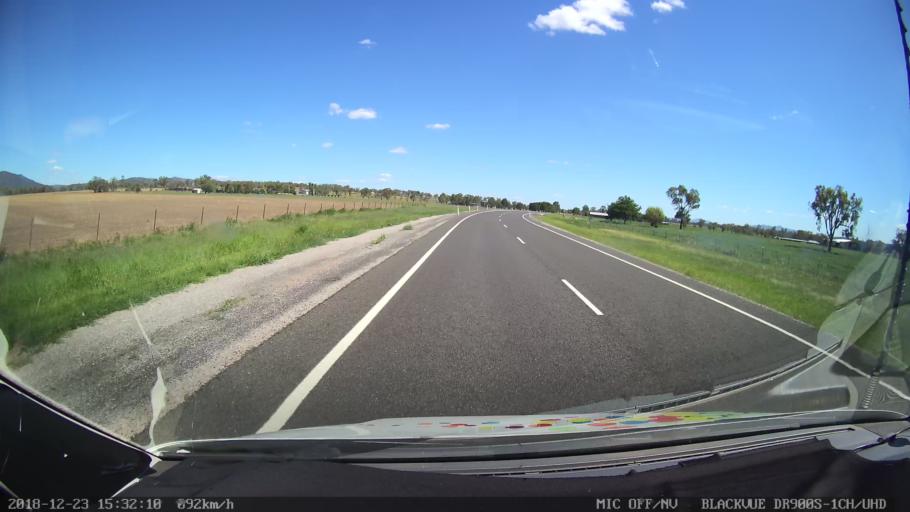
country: AU
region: New South Wales
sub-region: Tamworth Municipality
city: East Tamworth
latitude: -30.9818
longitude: 150.8701
